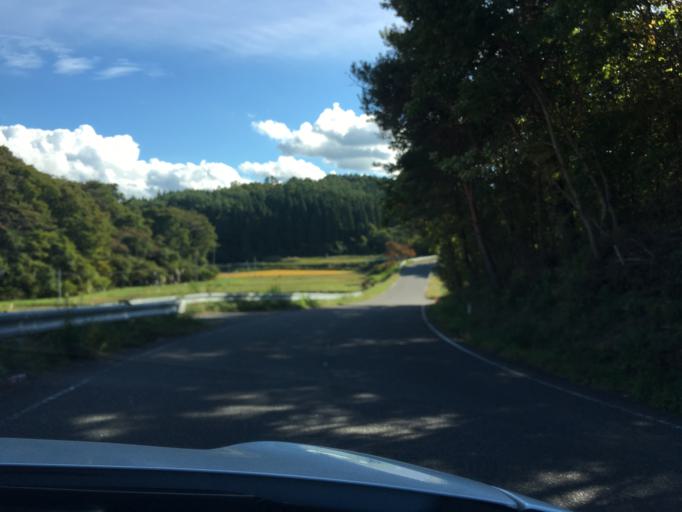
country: JP
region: Fukushima
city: Ishikawa
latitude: 37.1504
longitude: 140.5960
